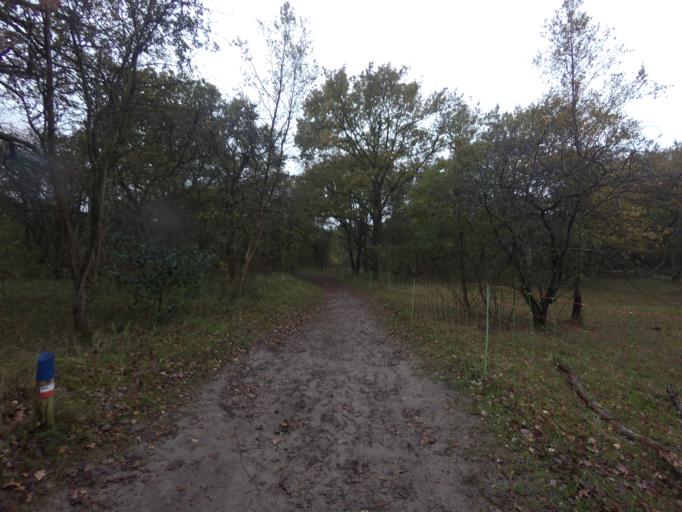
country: NL
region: South Holland
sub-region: Gemeente Wassenaar
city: Wassenaar
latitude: 52.1334
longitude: 4.3457
